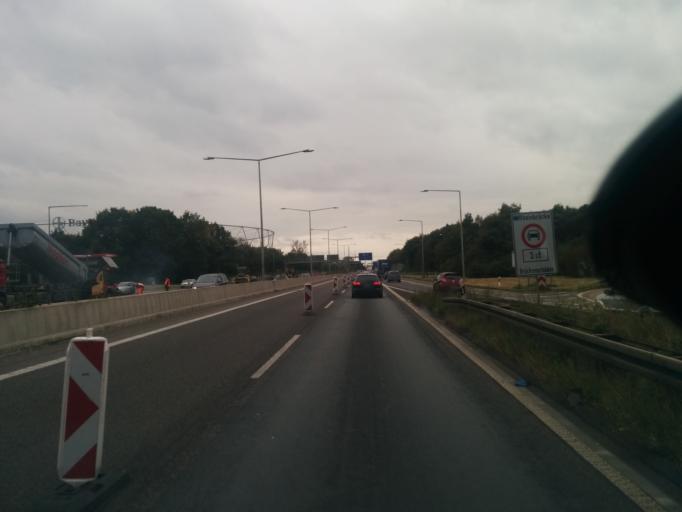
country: DE
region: North Rhine-Westphalia
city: Opladen
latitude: 51.0416
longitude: 7.0065
